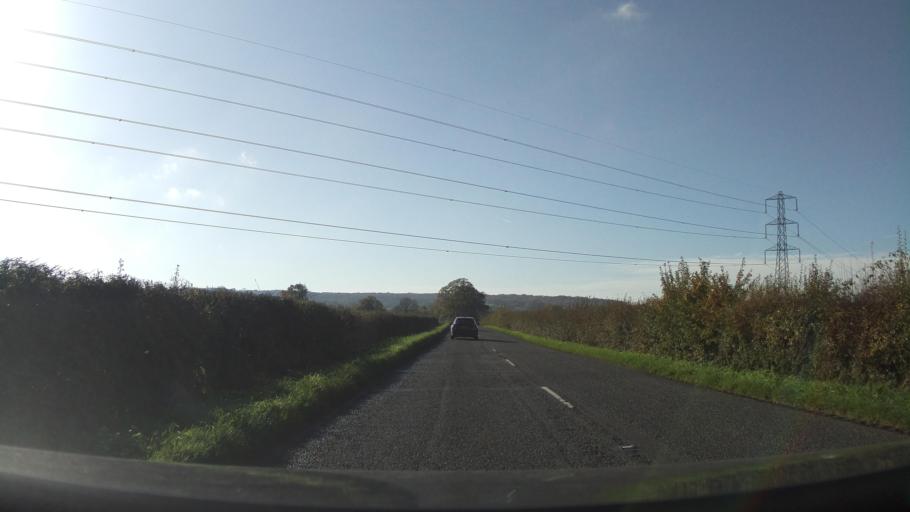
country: GB
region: England
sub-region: Somerset
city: Bruton
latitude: 51.1814
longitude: -2.4060
